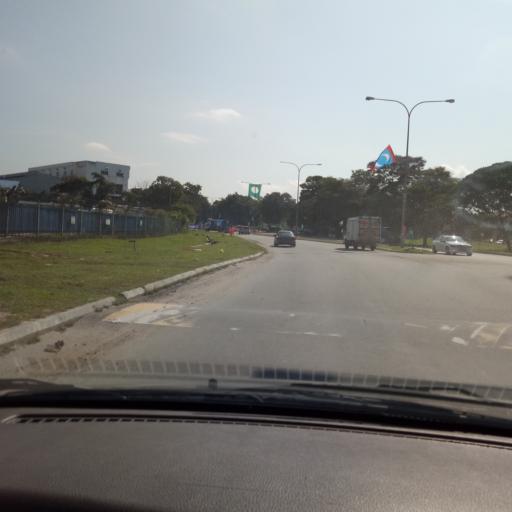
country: MY
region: Selangor
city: Kampong Baharu Balakong
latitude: 3.0182
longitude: 101.7643
